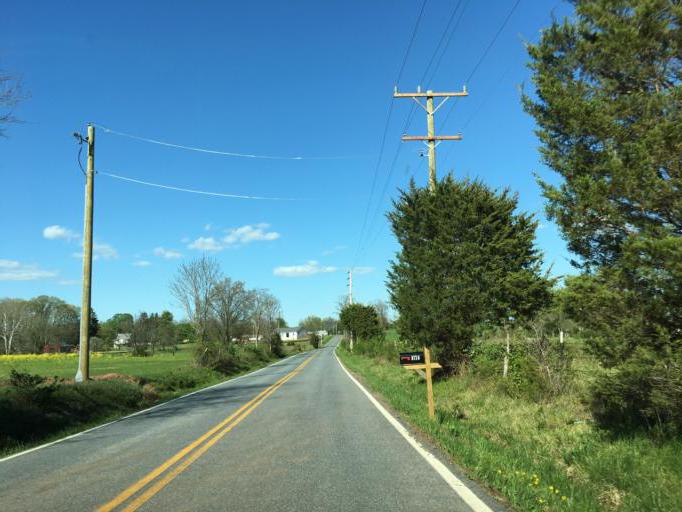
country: US
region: Maryland
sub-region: Frederick County
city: Thurmont
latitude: 39.6576
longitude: -77.3642
